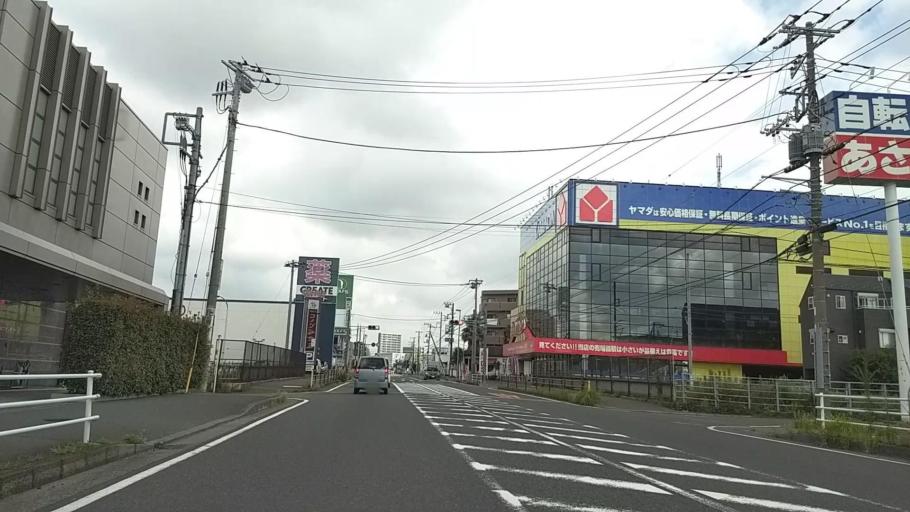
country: JP
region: Kanagawa
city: Minami-rinkan
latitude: 35.5105
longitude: 139.4600
